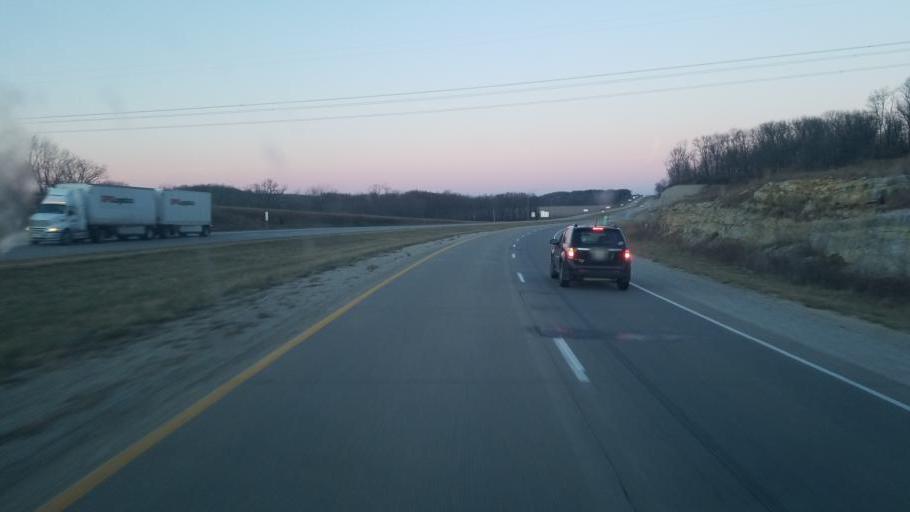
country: US
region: Iowa
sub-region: Henry County
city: Mount Pleasant
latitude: 40.9694
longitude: -91.6345
